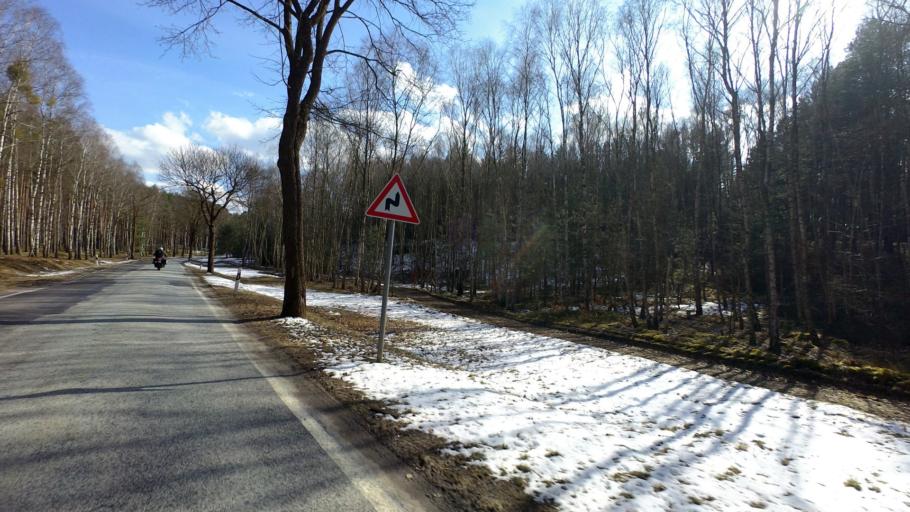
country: DE
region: Brandenburg
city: Biesenthal
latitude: 52.7921
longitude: 13.6031
